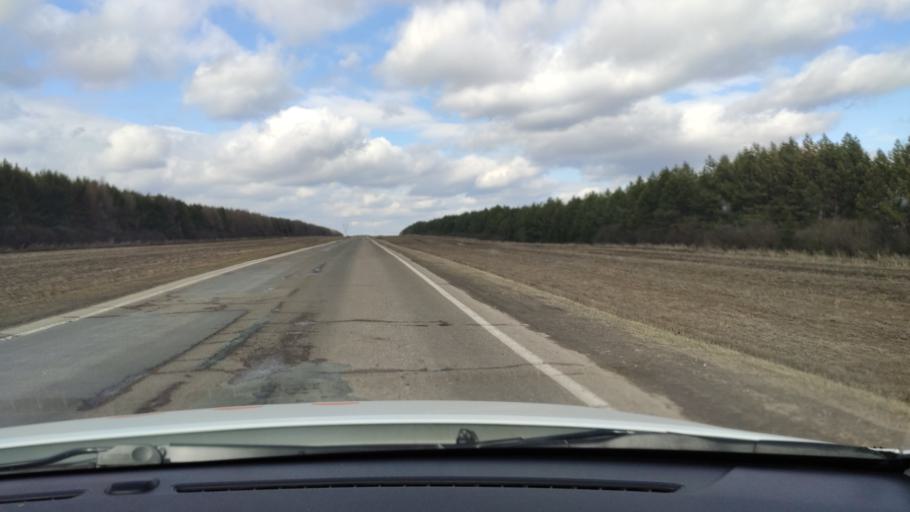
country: RU
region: Tatarstan
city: Vysokaya Gora
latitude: 56.1533
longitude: 49.2121
